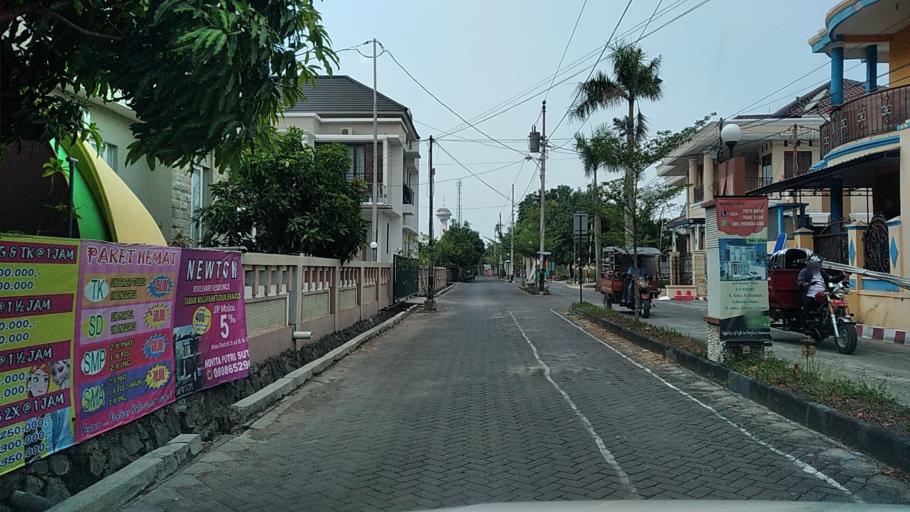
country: ID
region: Central Java
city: Semarang
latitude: -6.9931
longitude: 110.4447
